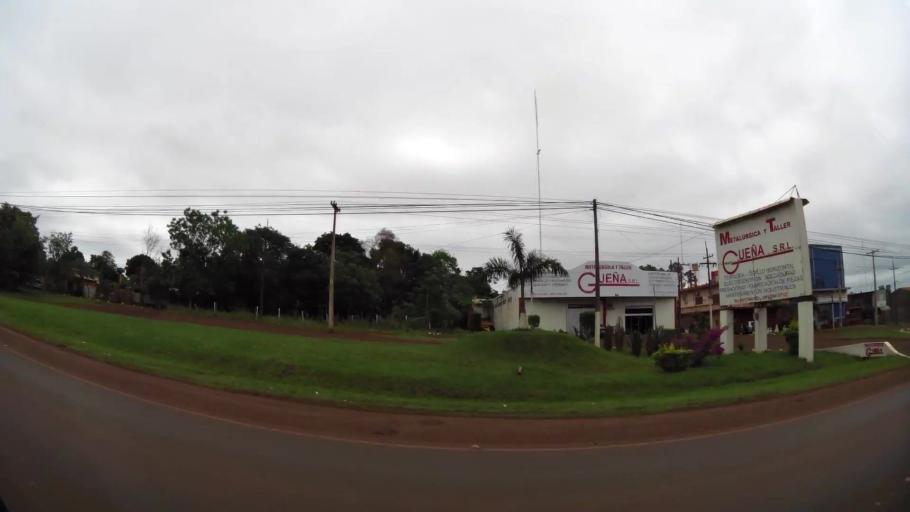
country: PY
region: Alto Parana
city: Los Cedrales
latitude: -25.4889
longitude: -54.8038
